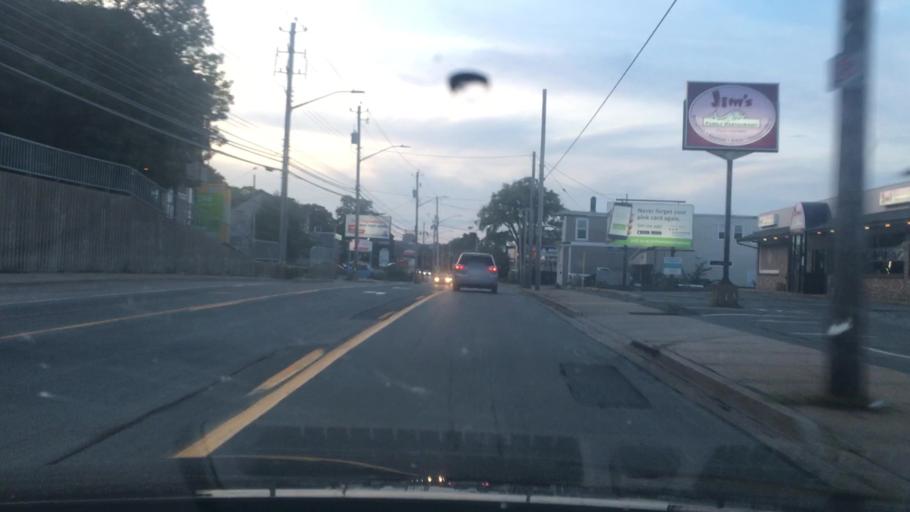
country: CA
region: Nova Scotia
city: Dartmouth
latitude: 44.6766
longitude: -63.6487
